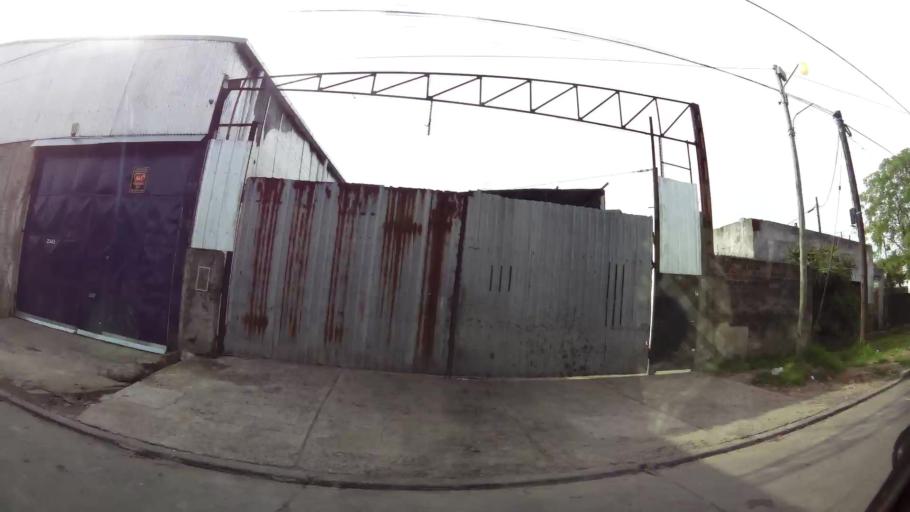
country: AR
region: Buenos Aires
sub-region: Partido de Quilmes
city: Quilmes
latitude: -34.7466
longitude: -58.2770
